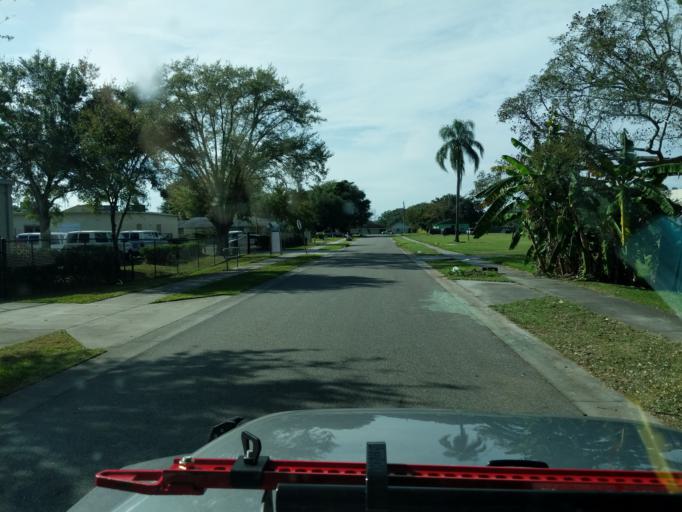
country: US
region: Florida
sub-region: Orange County
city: Winter Garden
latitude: 28.5669
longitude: -81.5651
